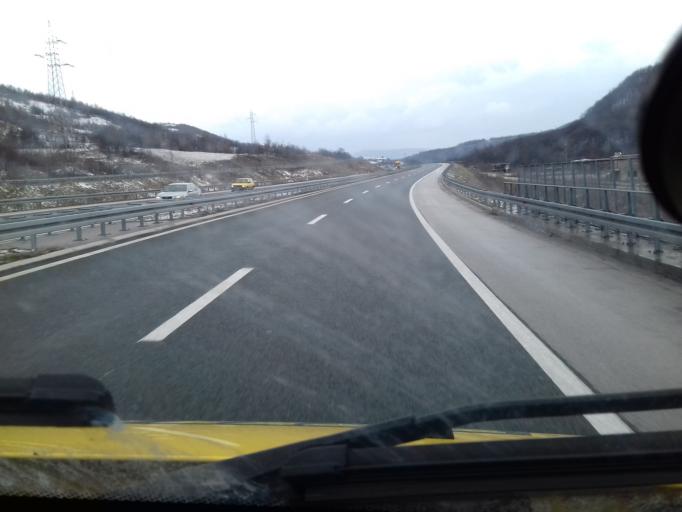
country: BA
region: Federation of Bosnia and Herzegovina
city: Kakanj
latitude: 44.1368
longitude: 18.0356
